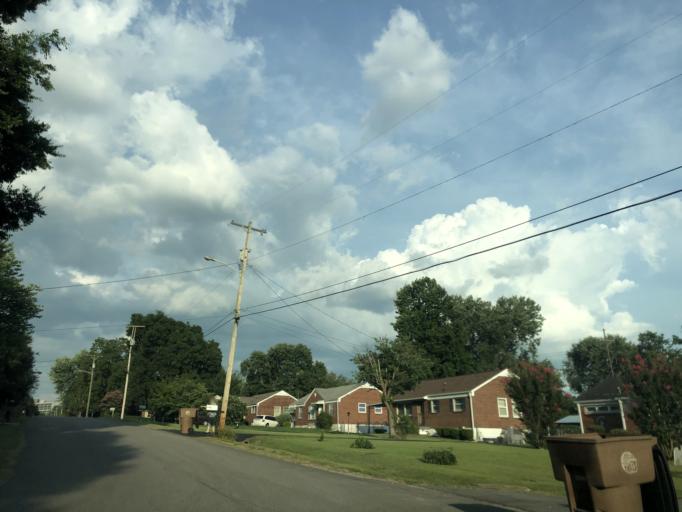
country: US
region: Tennessee
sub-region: Davidson County
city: Nashville
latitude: 36.1531
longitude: -86.6991
